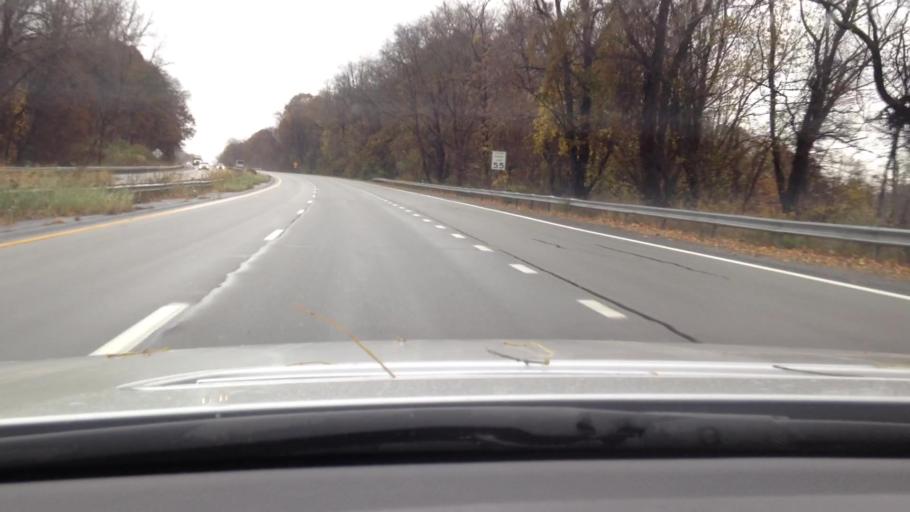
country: US
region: New York
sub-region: Westchester County
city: Buchanan
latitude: 41.2671
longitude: -73.9342
